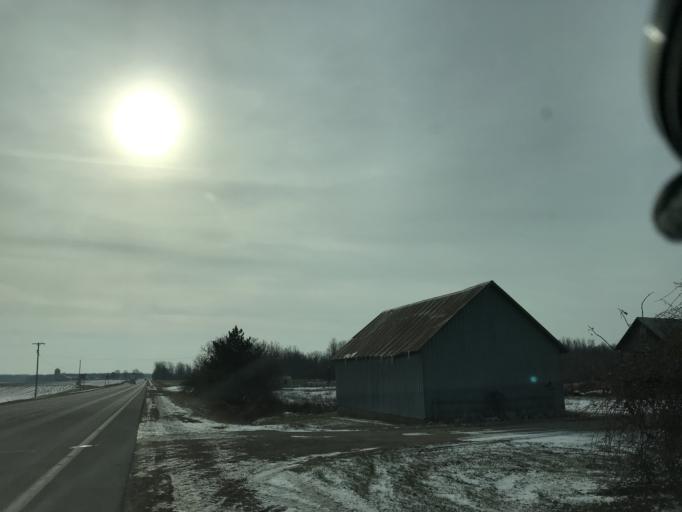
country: US
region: Michigan
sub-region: Ionia County
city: Lake Odessa
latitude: 42.7544
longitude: -85.0745
